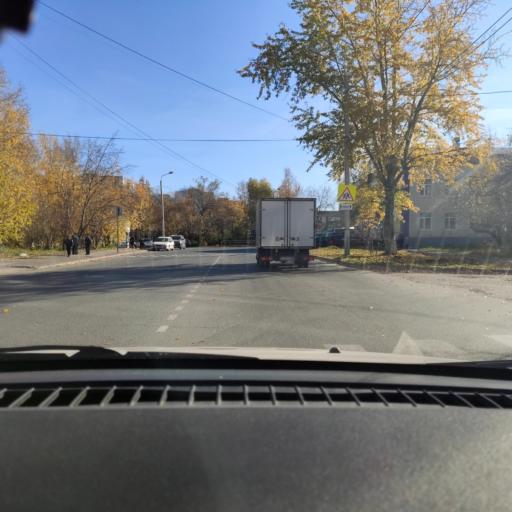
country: RU
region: Perm
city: Perm
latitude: 58.0677
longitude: 56.3560
